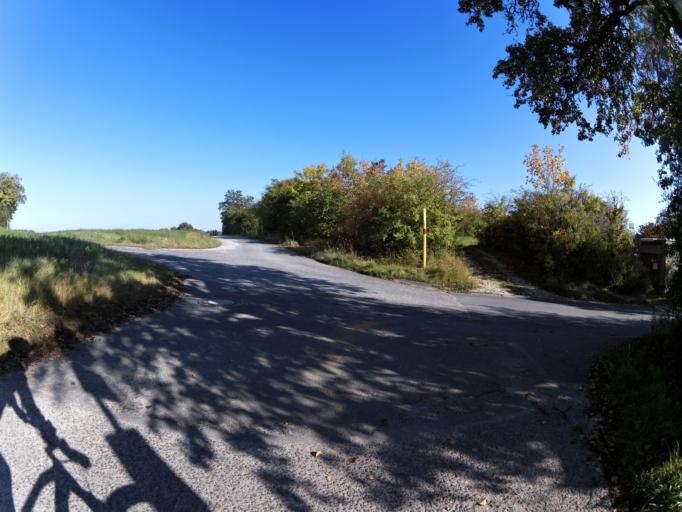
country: DE
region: Bavaria
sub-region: Regierungsbezirk Unterfranken
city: Ochsenfurt
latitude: 49.6746
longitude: 10.0665
